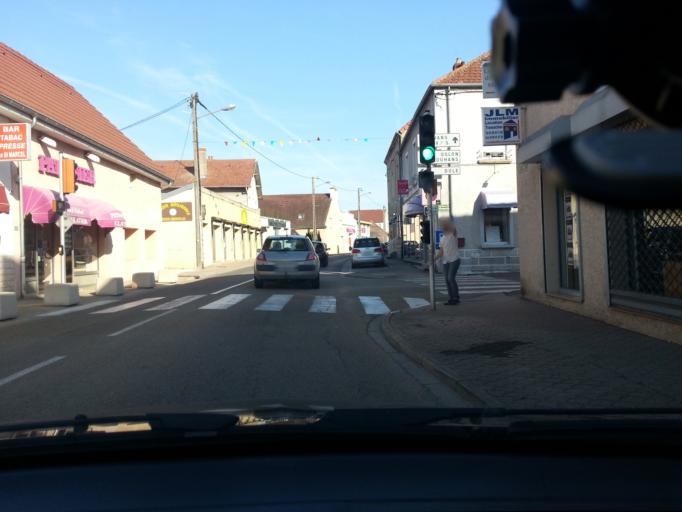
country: FR
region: Bourgogne
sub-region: Departement de Saone-et-Loire
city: Saint-Marcel
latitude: 46.7754
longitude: 4.8908
